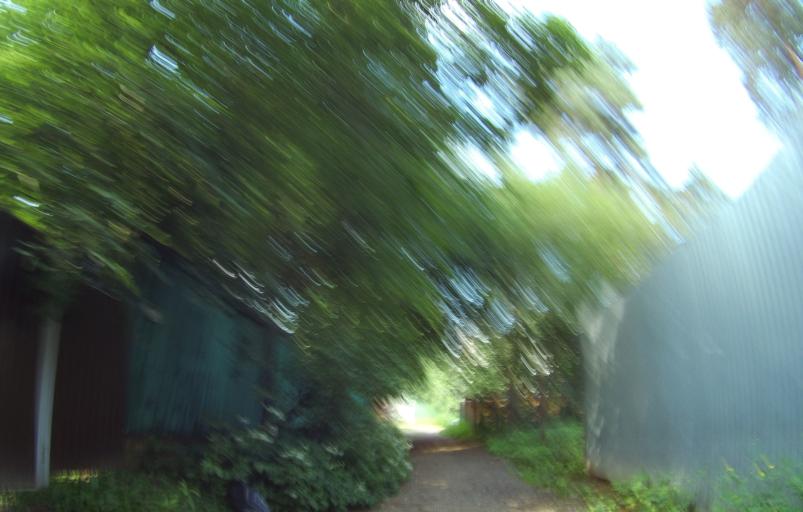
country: RU
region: Moskovskaya
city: Kraskovo
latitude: 55.6434
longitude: 37.9834
